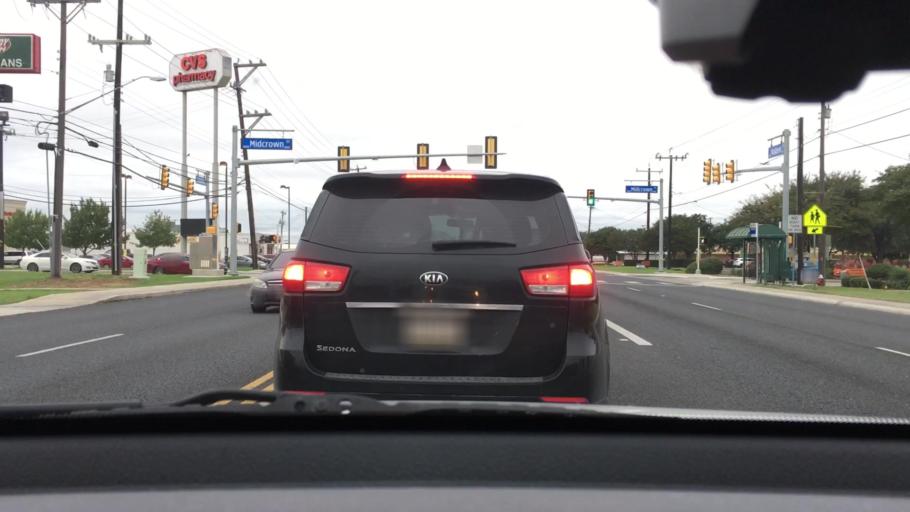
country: US
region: Texas
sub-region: Bexar County
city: Windcrest
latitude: 29.5103
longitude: -98.3798
